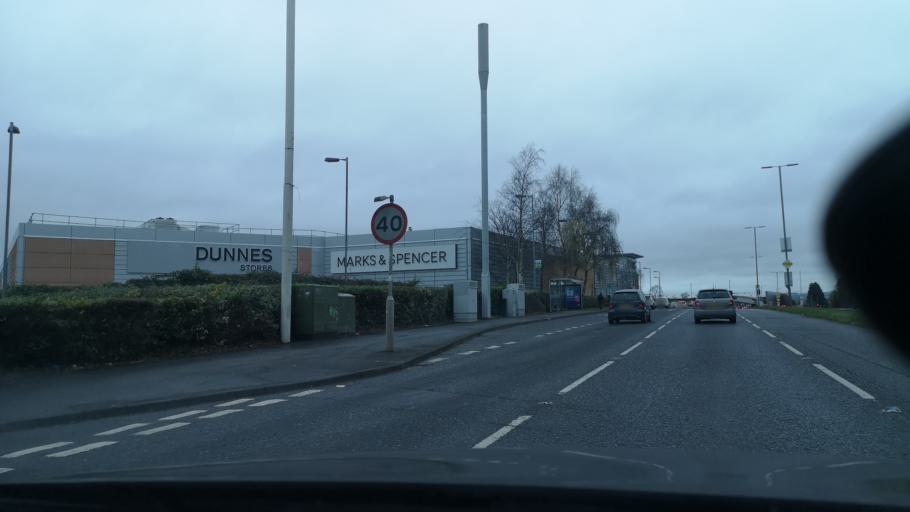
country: GB
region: Northern Ireland
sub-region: Castlereagh District
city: Castlereagh
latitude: 54.5620
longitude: -5.9091
